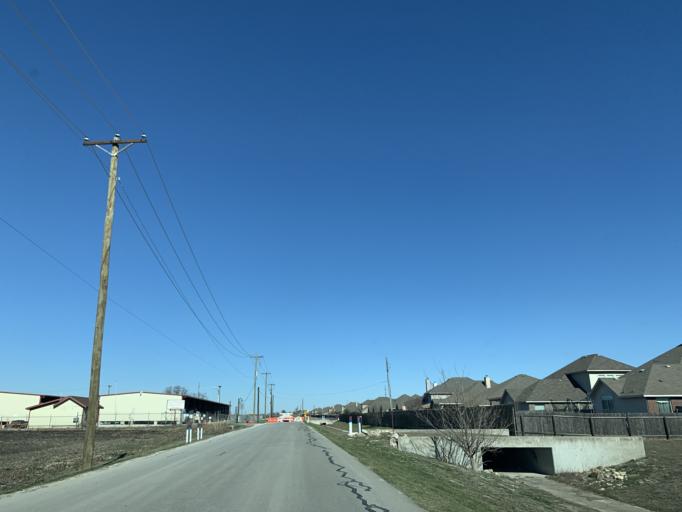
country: US
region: Texas
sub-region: Williamson County
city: Hutto
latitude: 30.5459
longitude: -97.5662
